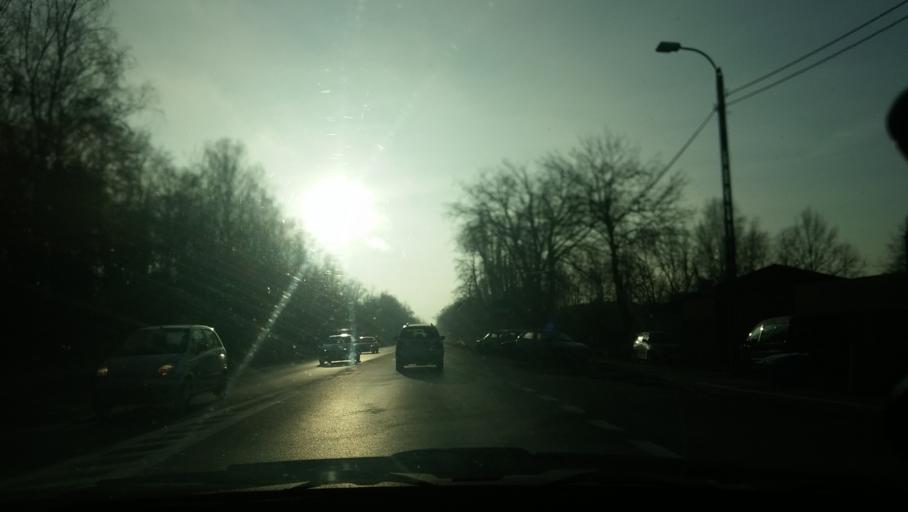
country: PL
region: Masovian Voivodeship
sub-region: Powiat minski
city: Sulejowek
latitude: 52.2224
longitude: 21.2500
